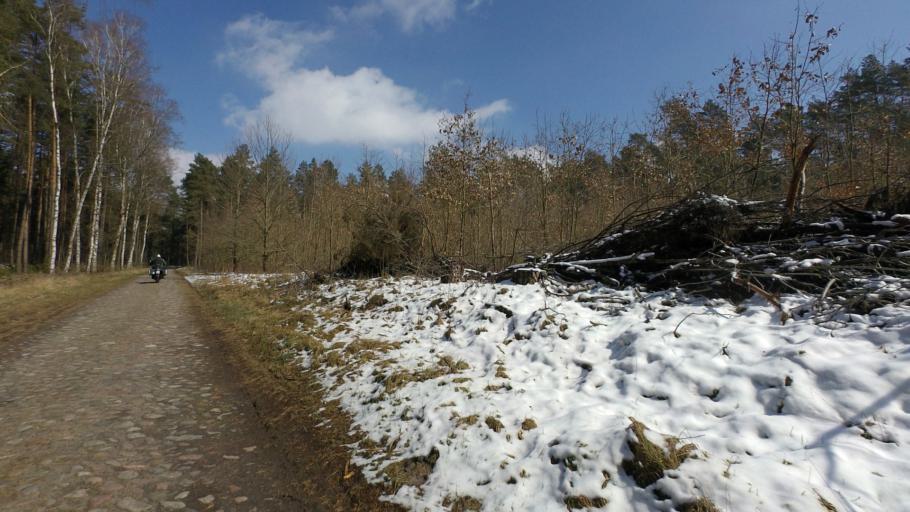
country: DE
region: Brandenburg
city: Werftpfuhl
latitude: 52.7072
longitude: 13.7859
